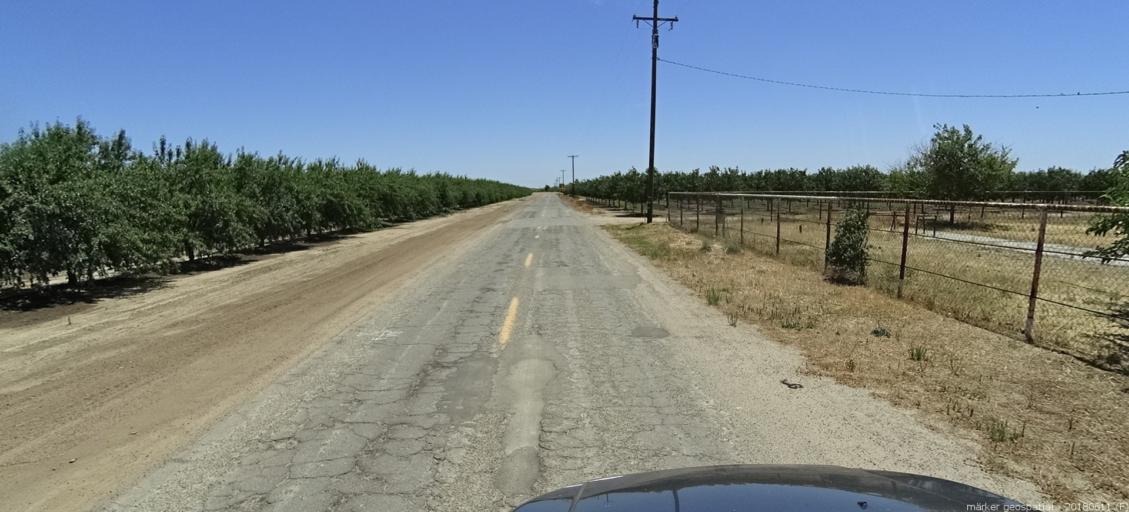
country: US
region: California
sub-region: Madera County
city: Fairmead
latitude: 37.0214
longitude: -120.2114
